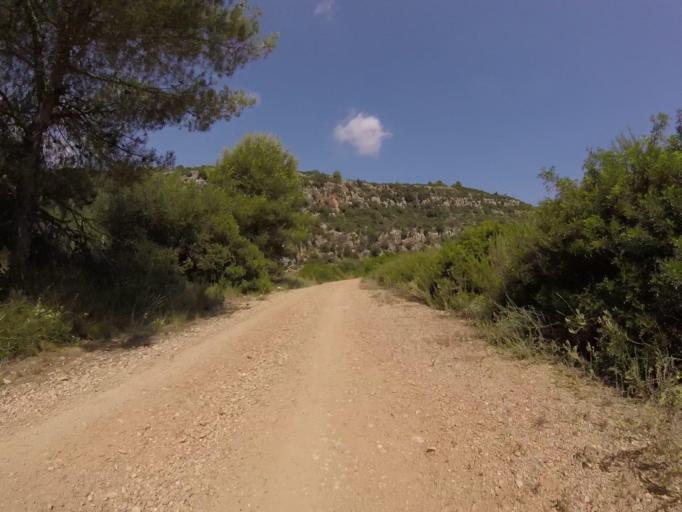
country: ES
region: Valencia
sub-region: Provincia de Castello
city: Torreblanca
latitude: 40.2208
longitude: 0.1475
